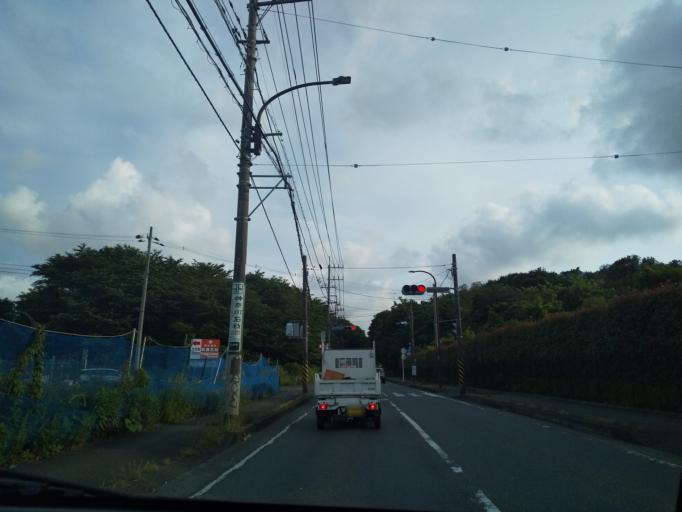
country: JP
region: Kanagawa
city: Zama
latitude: 35.5173
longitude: 139.3935
